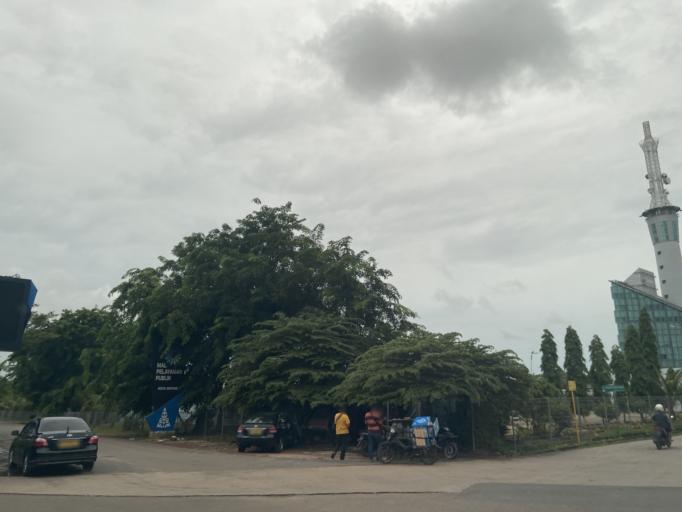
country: SG
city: Singapore
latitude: 1.1302
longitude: 104.0567
